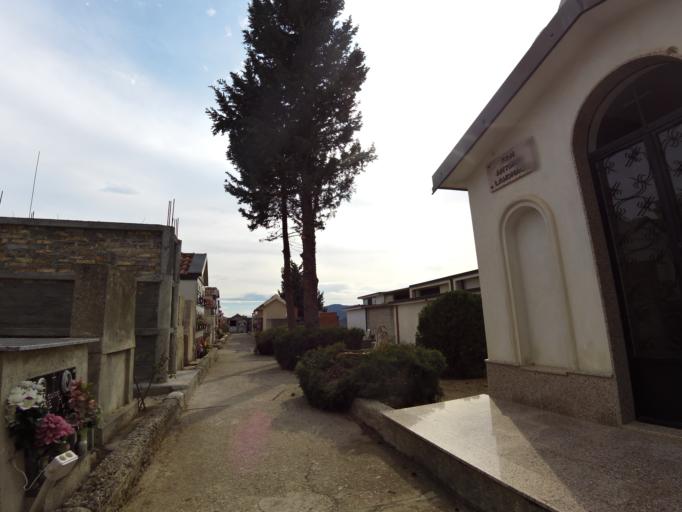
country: IT
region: Calabria
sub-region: Provincia di Reggio Calabria
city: Stignano
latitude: 38.4228
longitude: 16.4669
